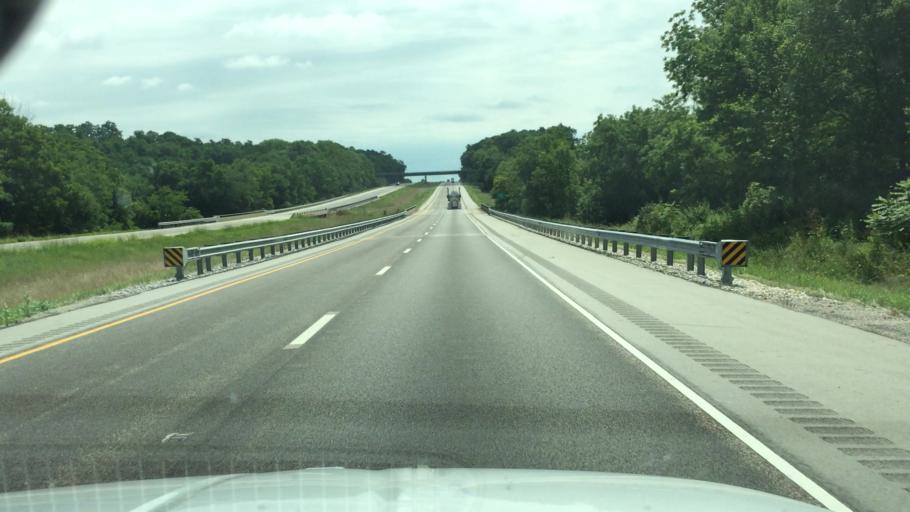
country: US
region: Illinois
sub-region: Peoria County
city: Elmwood
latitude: 40.8600
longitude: -90.0100
